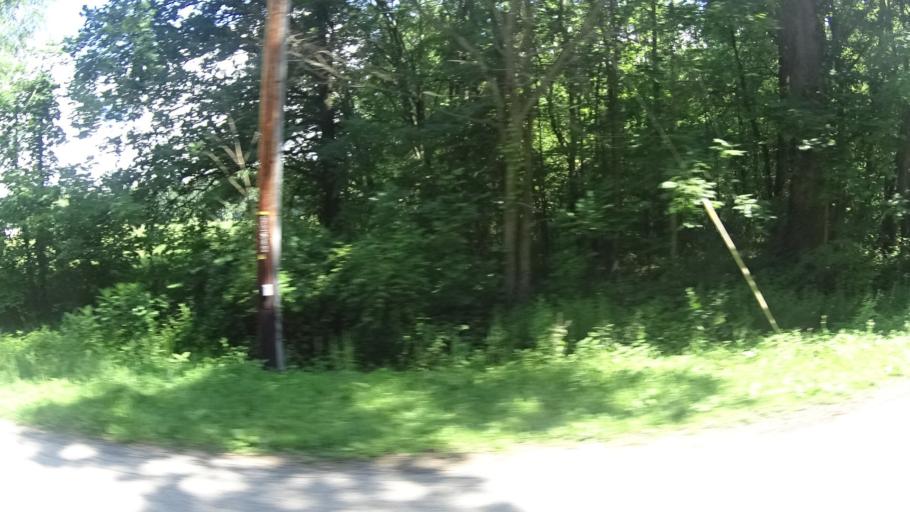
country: US
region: Ohio
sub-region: Huron County
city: Wakeman
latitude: 41.2839
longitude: -82.4330
